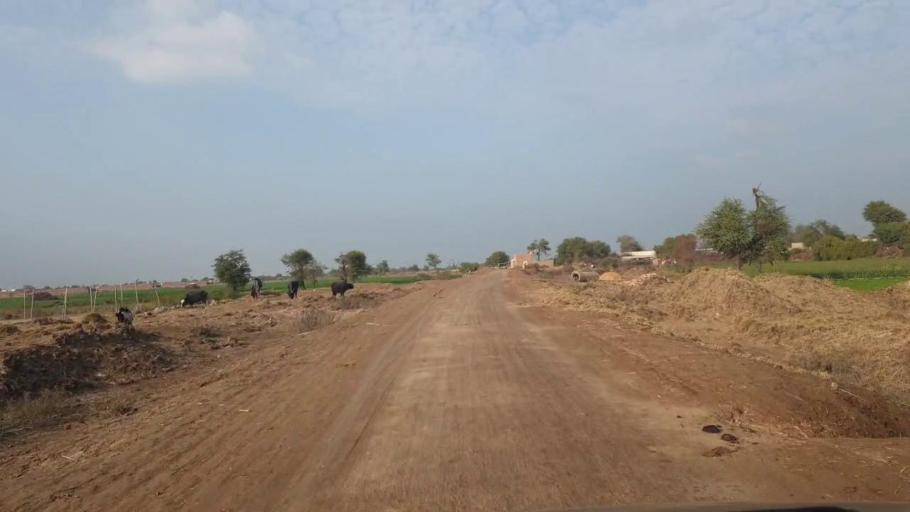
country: PK
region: Sindh
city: Shahdadpur
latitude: 25.8763
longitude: 68.7161
